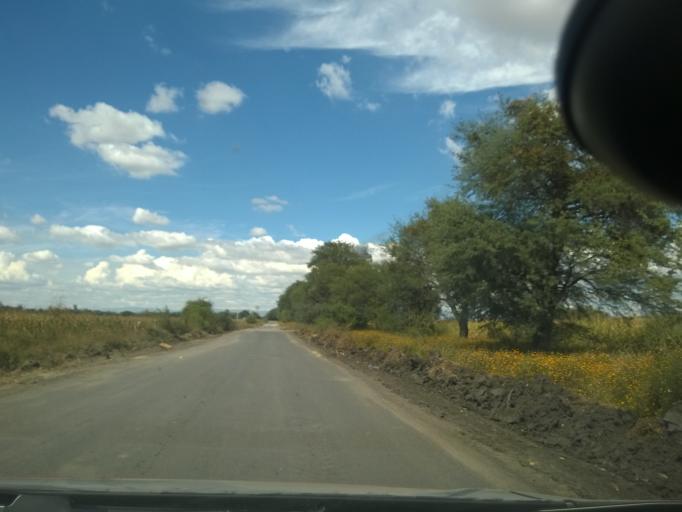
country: MX
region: Guanajuato
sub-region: Leon
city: Plan Guanajuato (La Sandia)
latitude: 20.9003
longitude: -101.6311
